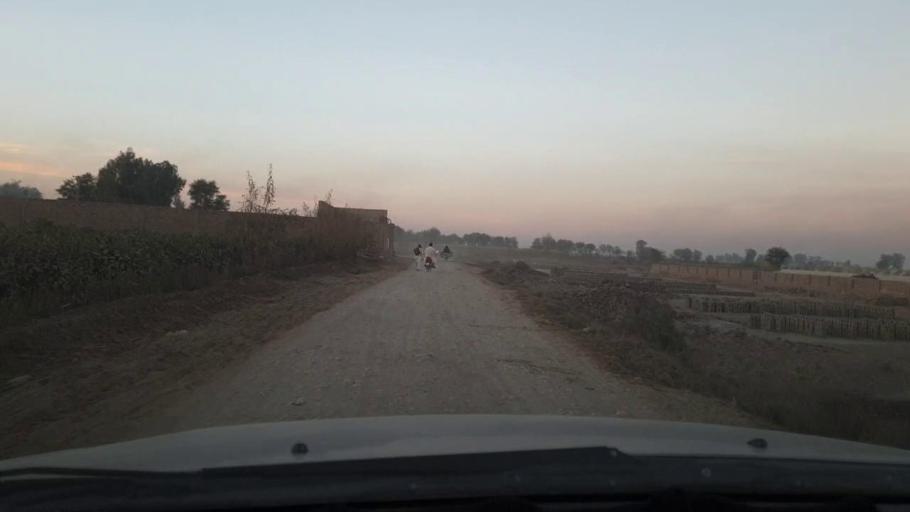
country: PK
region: Sindh
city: Ghotki
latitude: 27.9805
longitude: 69.2840
